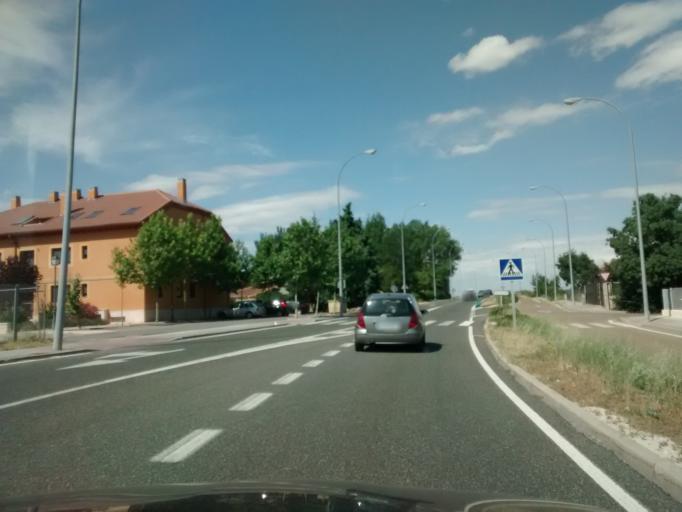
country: ES
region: Castille and Leon
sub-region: Provincia de Segovia
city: Torrecaballeros
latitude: 40.9940
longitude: -4.0228
